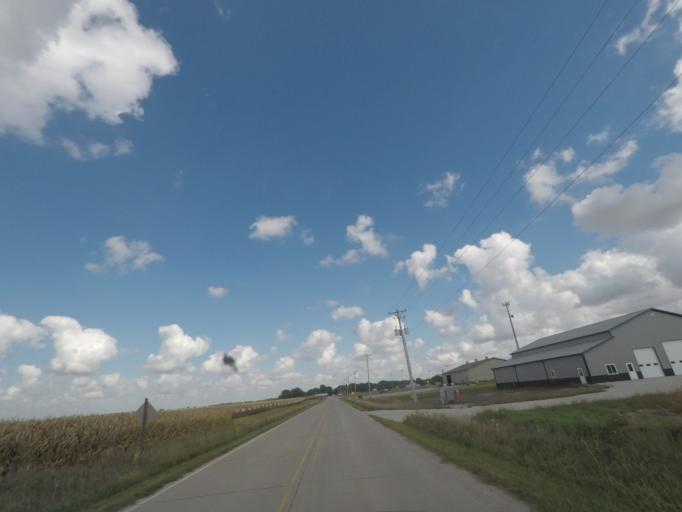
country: US
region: Iowa
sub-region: Story County
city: Nevada
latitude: 42.0048
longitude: -93.3190
